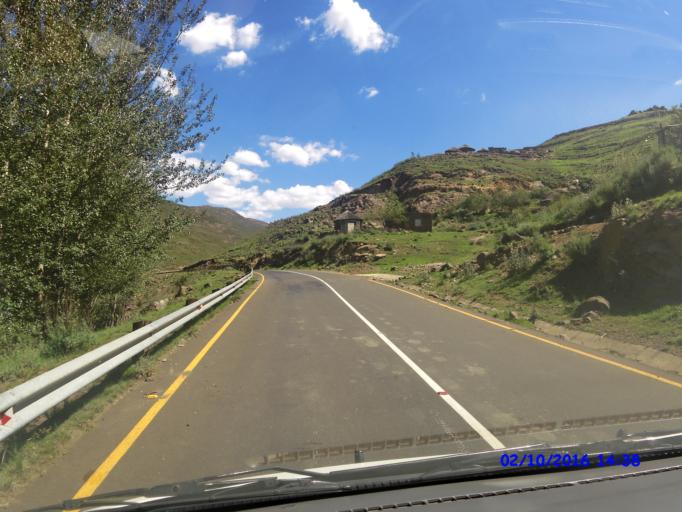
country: LS
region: Maseru
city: Nako
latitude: -29.5060
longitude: 28.0629
